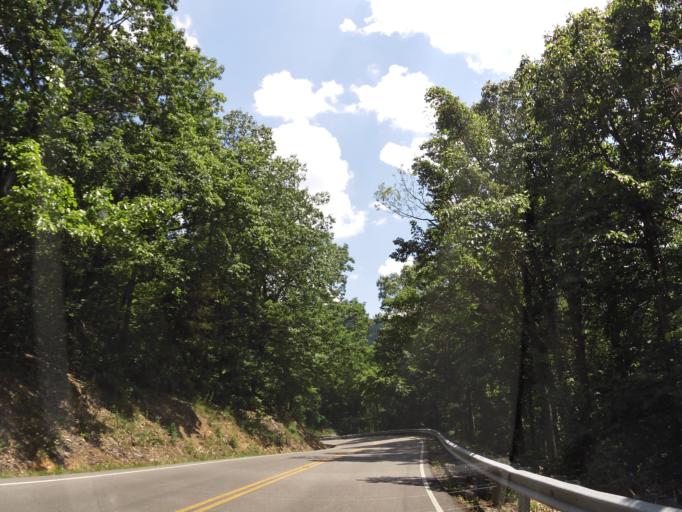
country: US
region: Tennessee
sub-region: Bledsoe County
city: Pikeville
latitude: 35.5742
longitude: -85.1539
